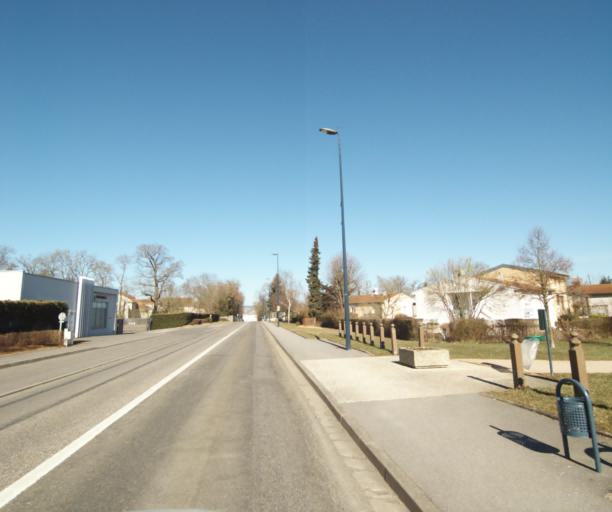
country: FR
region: Lorraine
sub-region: Departement de Meurthe-et-Moselle
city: Jarville-la-Malgrange
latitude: 48.6639
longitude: 6.2077
